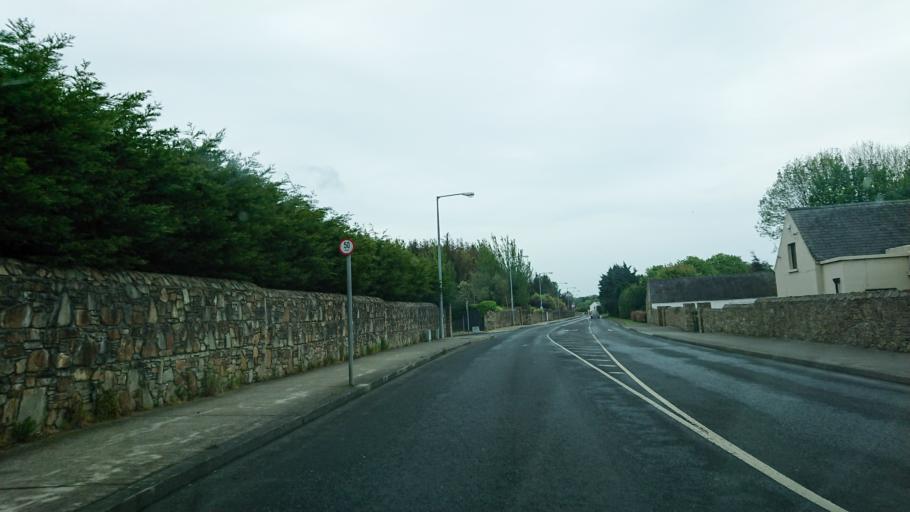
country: IE
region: Munster
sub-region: Waterford
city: Waterford
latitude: 52.2339
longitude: -7.0733
